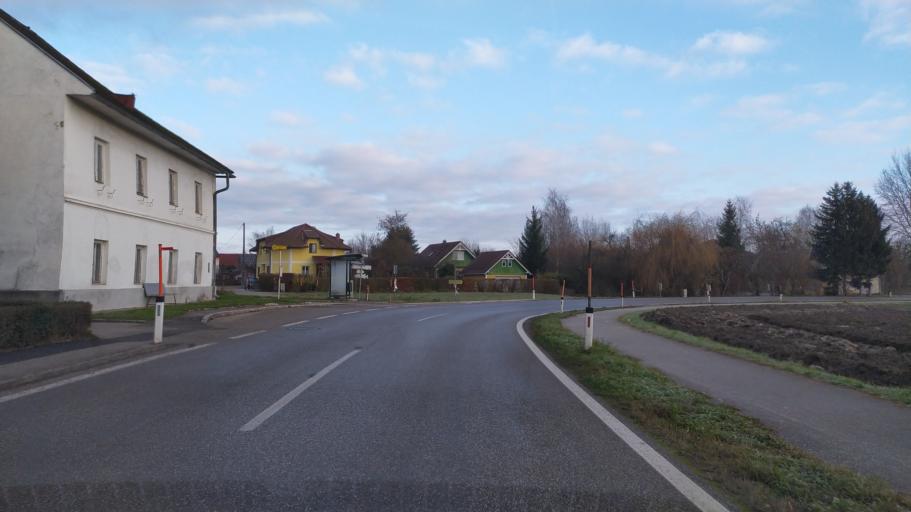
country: AT
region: Upper Austria
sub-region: Politischer Bezirk Perg
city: Perg
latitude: 48.2282
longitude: 14.5918
